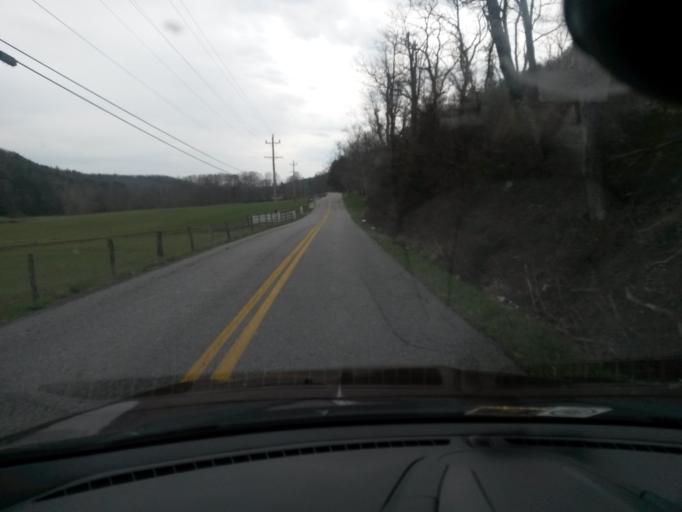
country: US
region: Virginia
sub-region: Bath County
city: Warm Springs
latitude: 37.9954
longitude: -79.8892
